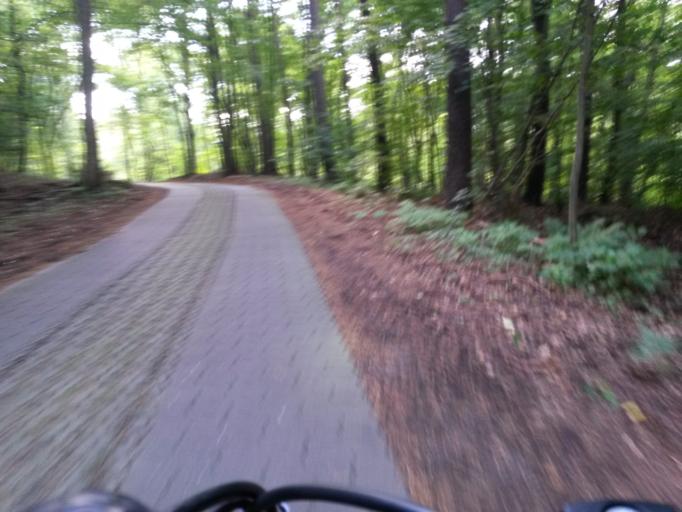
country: DE
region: Brandenburg
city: Althuttendorf
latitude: 53.0228
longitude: 13.8677
